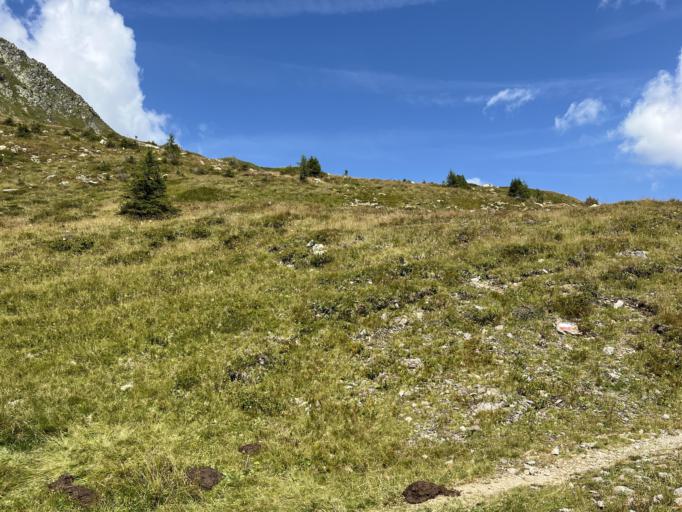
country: IT
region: Friuli Venezia Giulia
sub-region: Provincia di Udine
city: Forni Avoltri
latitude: 46.6271
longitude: 12.8117
